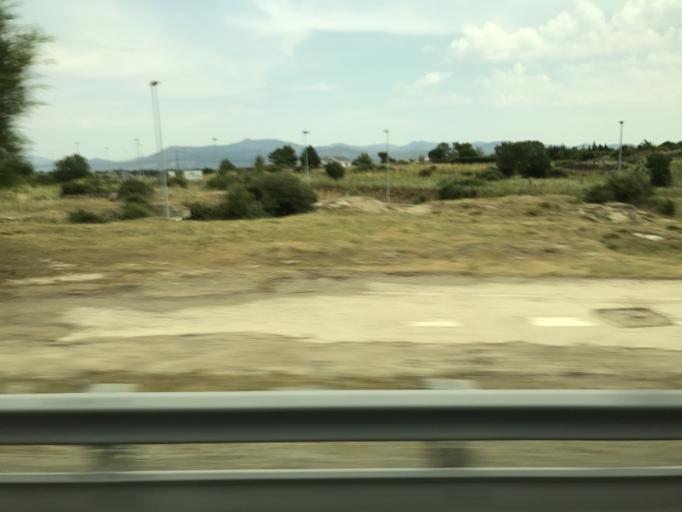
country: ES
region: Madrid
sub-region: Provincia de Madrid
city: La Cabrera
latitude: 40.9208
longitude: -3.6122
